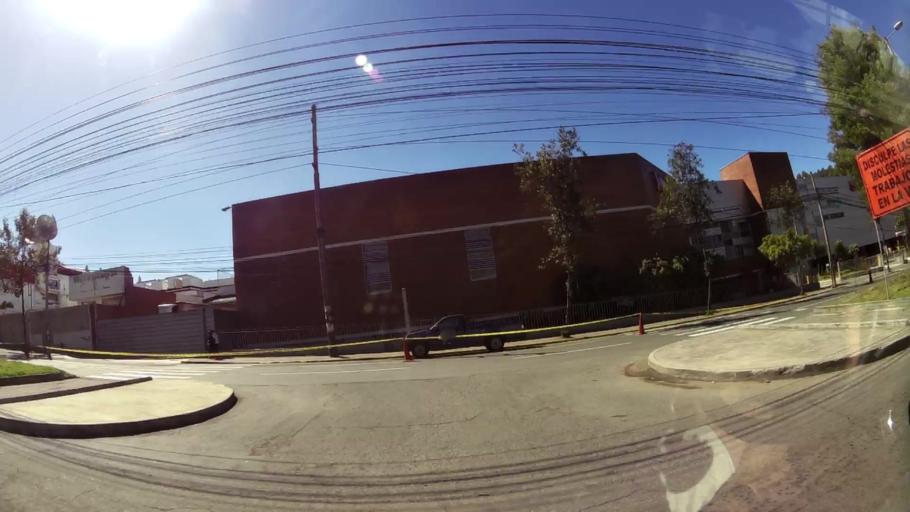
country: EC
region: Pichincha
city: Quito
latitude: -0.1635
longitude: -78.4677
